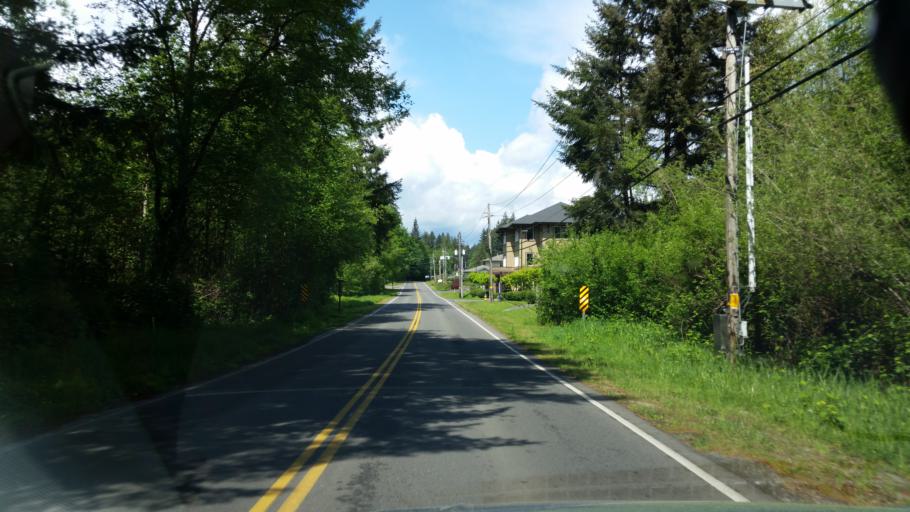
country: US
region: Washington
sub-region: Pierce County
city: Purdy
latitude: 47.3613
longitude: -122.6169
